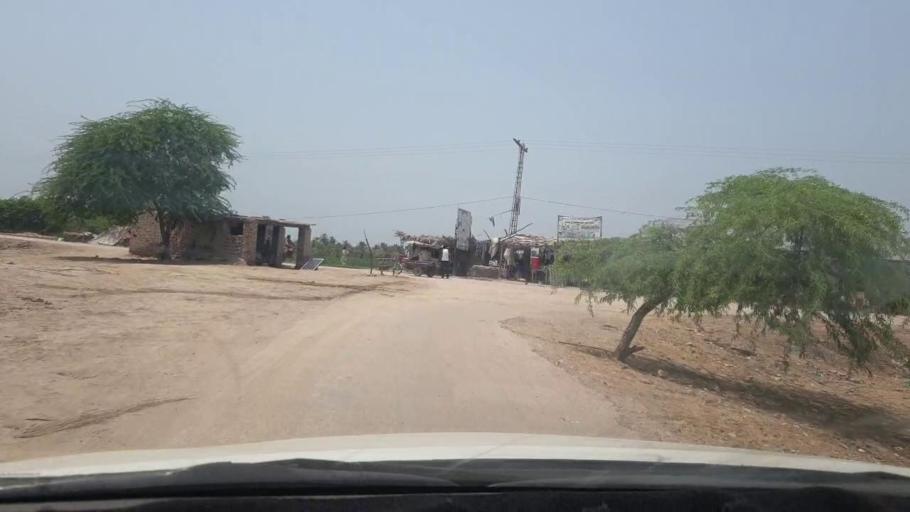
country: PK
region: Sindh
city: Khairpur
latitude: 27.5067
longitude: 68.8588
